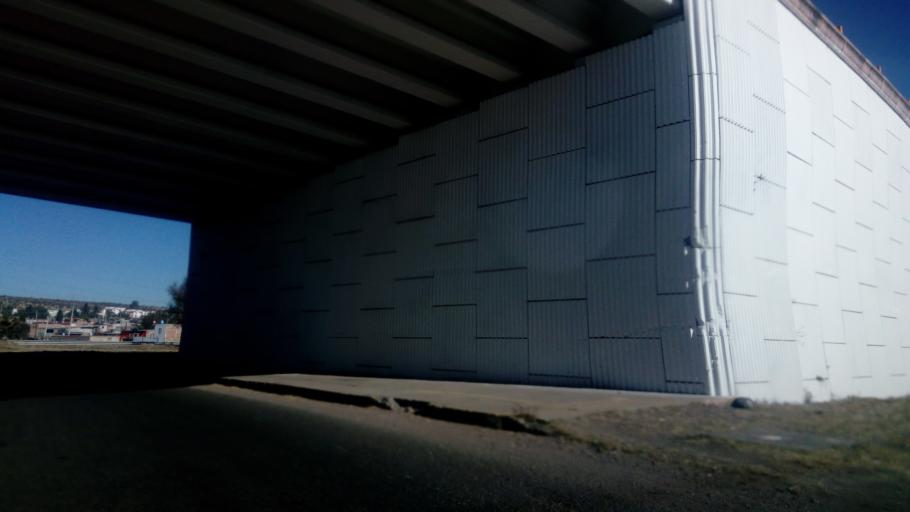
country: MX
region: Durango
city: Victoria de Durango
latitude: 24.0957
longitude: -104.5737
